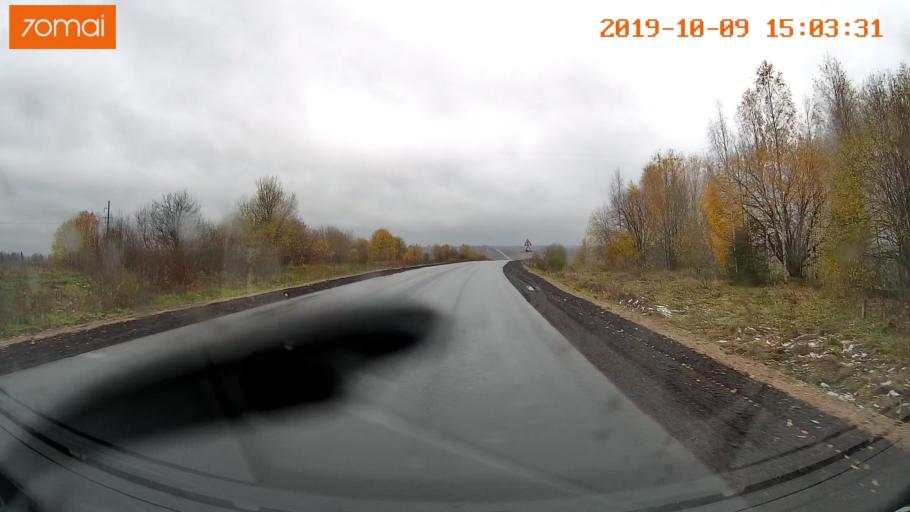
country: RU
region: Kostroma
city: Chistyye Bory
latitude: 58.2703
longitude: 41.6754
